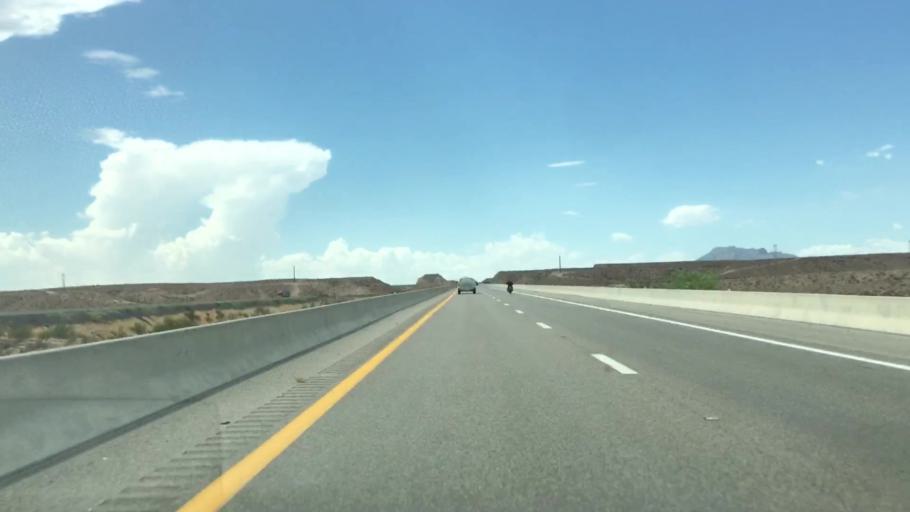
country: US
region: Nevada
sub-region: Clark County
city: Bunkerville
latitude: 36.7660
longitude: -114.1925
